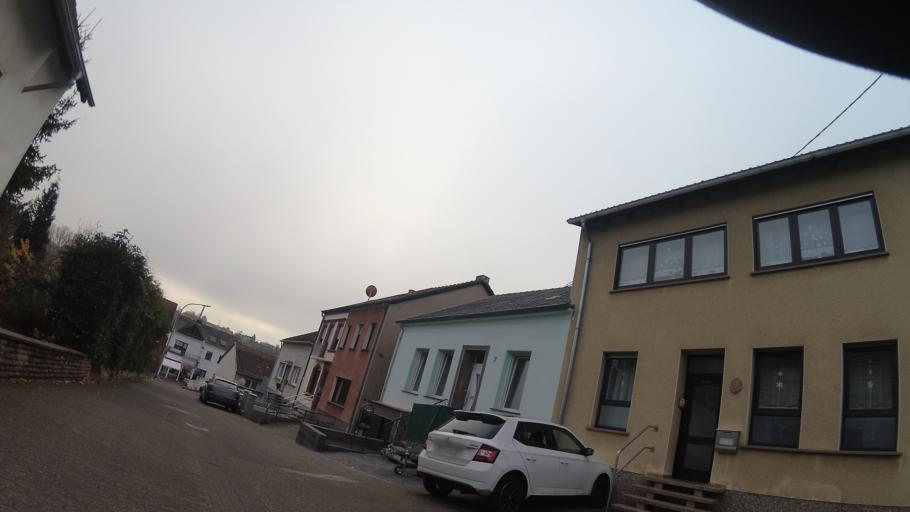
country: DE
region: Saarland
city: Schwalbach
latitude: 49.2978
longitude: 6.8037
